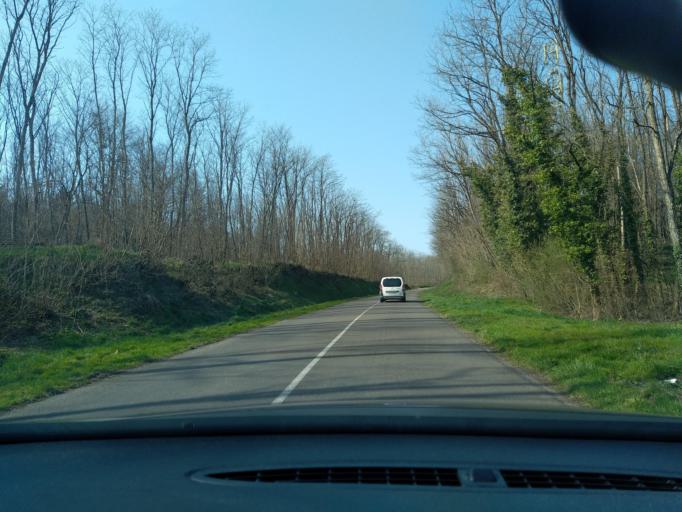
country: FR
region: Franche-Comte
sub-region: Departement du Jura
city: Dole
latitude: 47.0456
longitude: 5.5191
